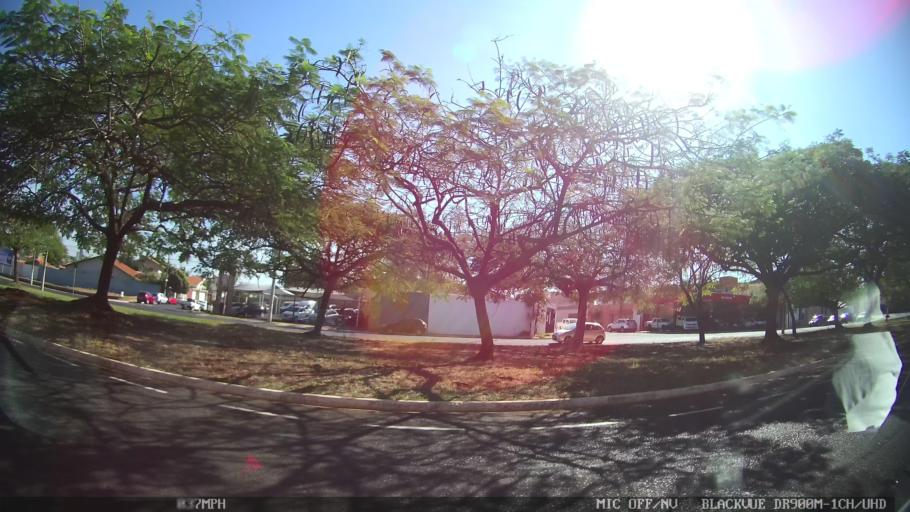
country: BR
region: Sao Paulo
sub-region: Ribeirao Preto
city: Ribeirao Preto
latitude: -21.2083
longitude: -47.7703
